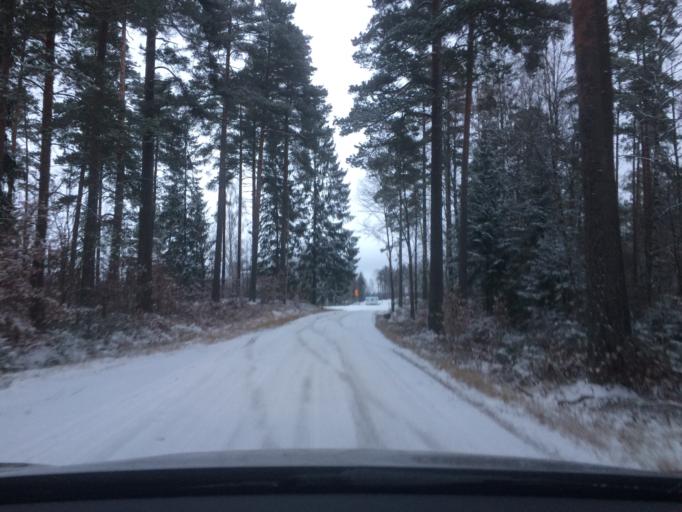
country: SE
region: Kronoberg
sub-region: Vaxjo Kommun
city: Vaexjoe
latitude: 56.8552
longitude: 14.7604
